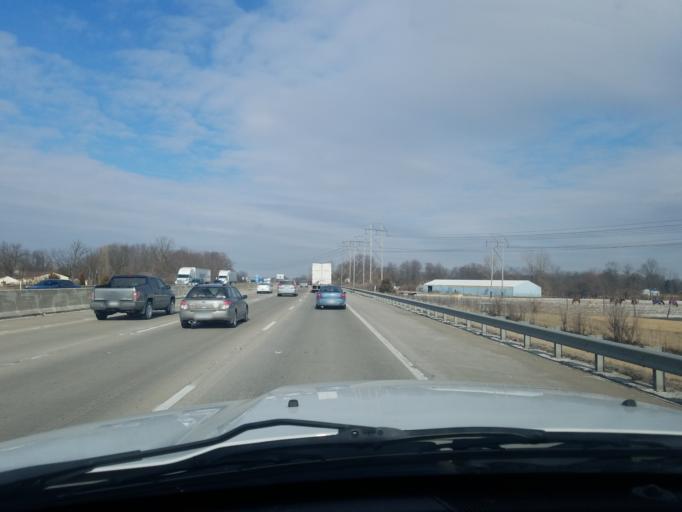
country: US
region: Indiana
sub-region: Marion County
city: Beech Grove
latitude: 39.7171
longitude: -86.0521
